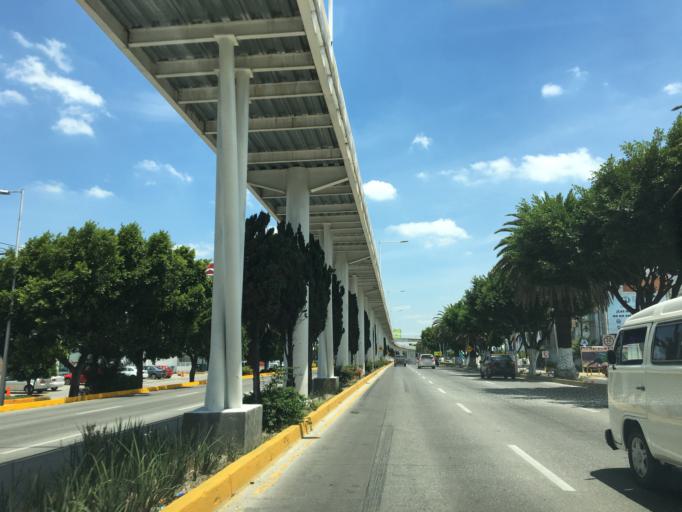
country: MX
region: Puebla
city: Puebla
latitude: 19.0693
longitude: -98.2253
